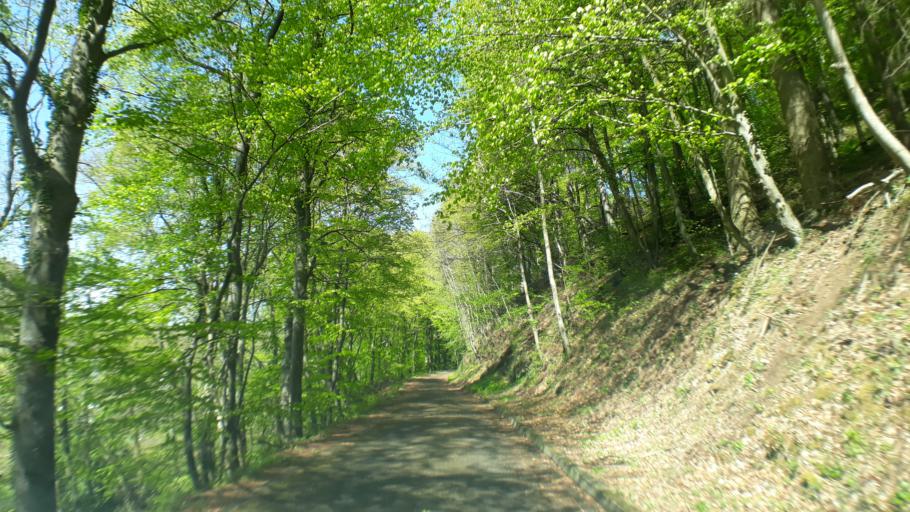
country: DE
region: North Rhine-Westphalia
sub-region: Regierungsbezirk Koln
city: Kall
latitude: 50.5052
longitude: 6.5753
